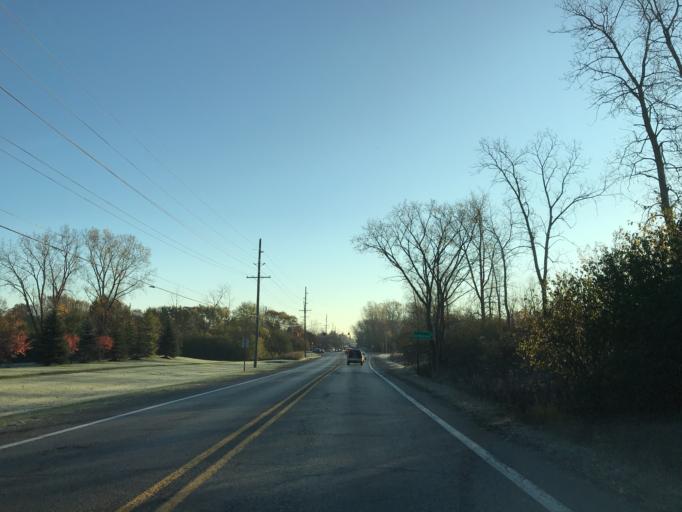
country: US
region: Michigan
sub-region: Oakland County
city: Wixom
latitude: 42.4647
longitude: -83.5367
